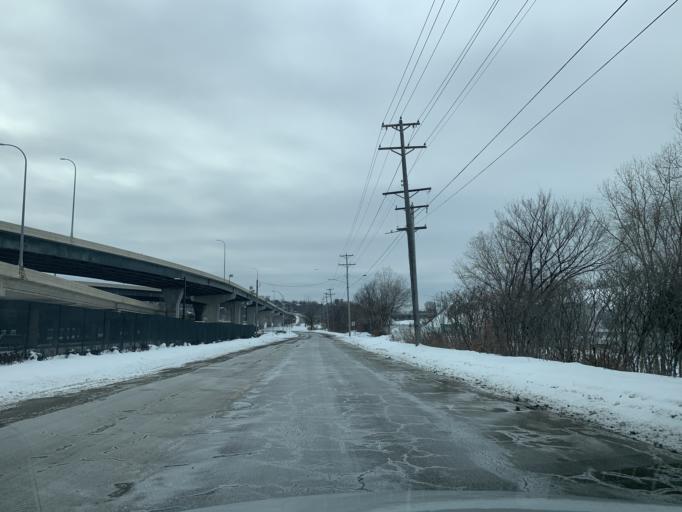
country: US
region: Minnesota
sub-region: Hennepin County
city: Minneapolis
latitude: 44.9754
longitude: -93.2915
